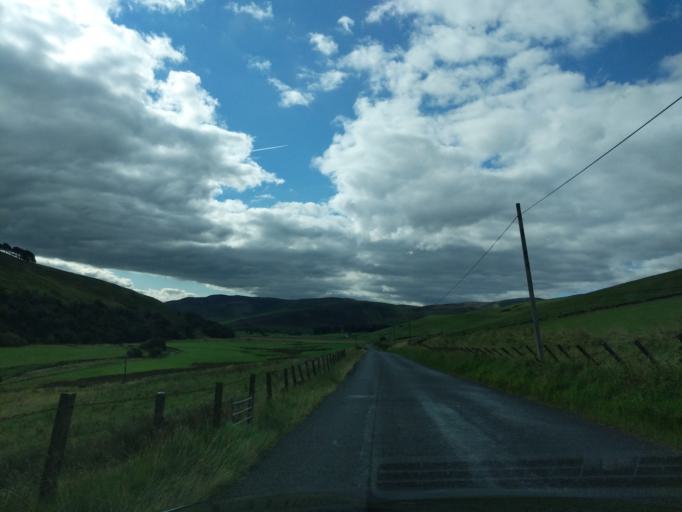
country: GB
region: Scotland
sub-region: The Scottish Borders
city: West Linton
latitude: 55.6916
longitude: -3.3339
